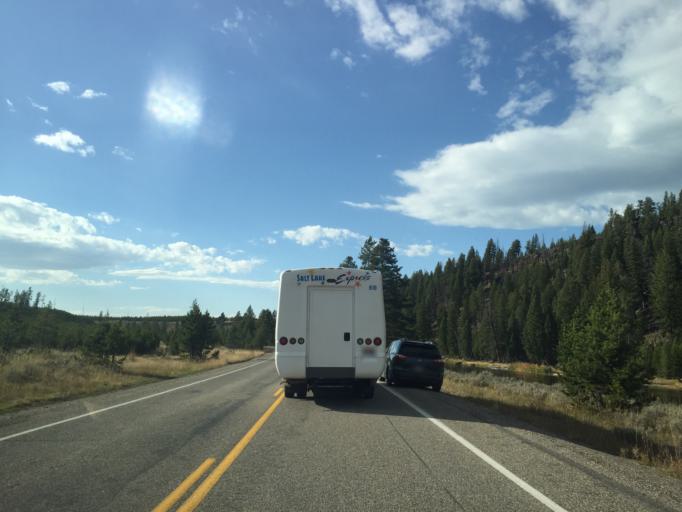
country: US
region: Montana
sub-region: Gallatin County
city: West Yellowstone
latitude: 44.6674
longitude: -110.9713
